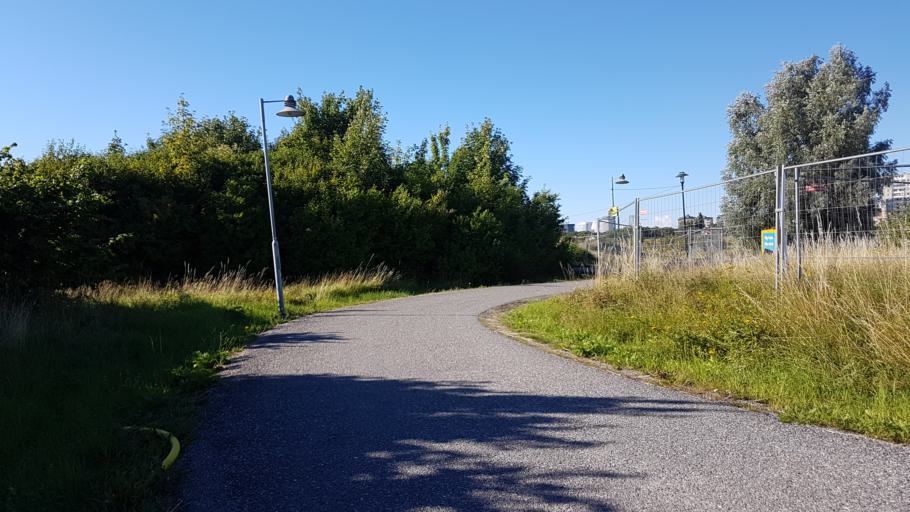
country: SE
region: Stockholm
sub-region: Stockholms Kommun
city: Arsta
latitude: 59.2911
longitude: 18.0413
